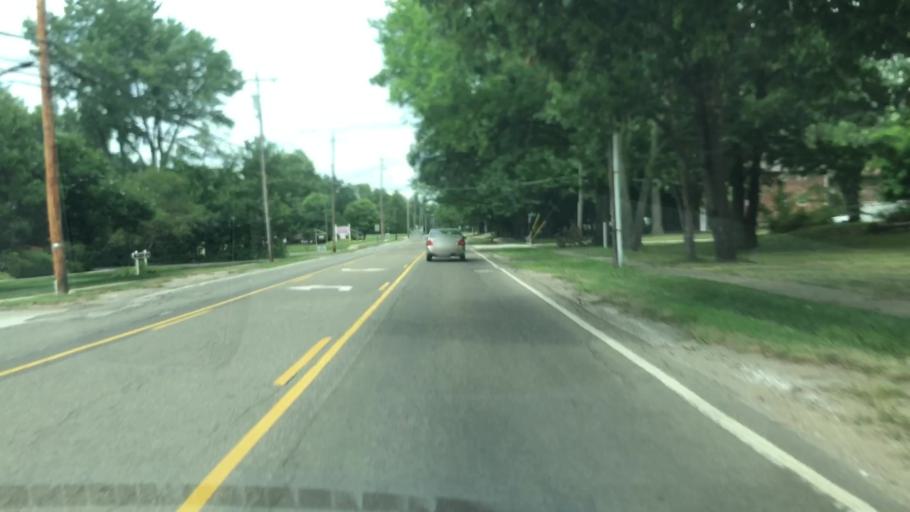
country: US
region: Ohio
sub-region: Summit County
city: Munroe Falls
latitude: 41.1492
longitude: -81.4404
